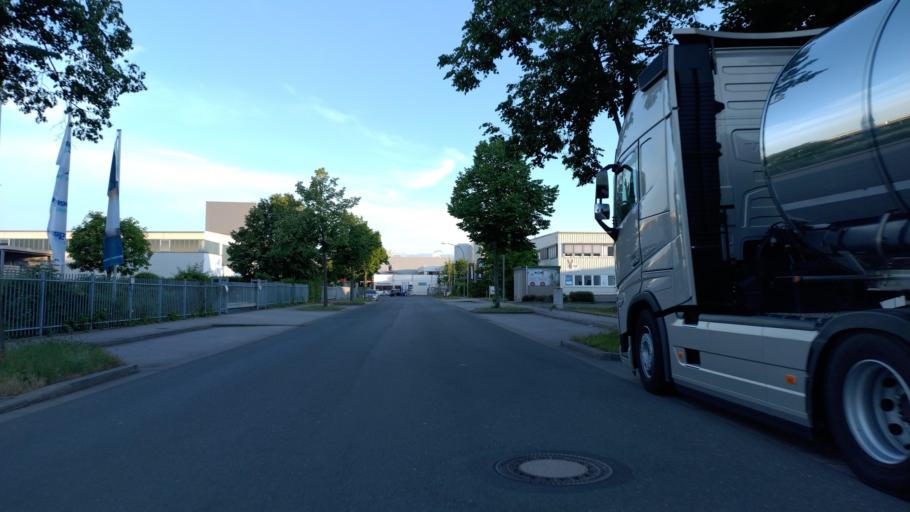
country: DE
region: Bavaria
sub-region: Upper Franconia
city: Bindlach
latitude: 49.9676
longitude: 11.6083
